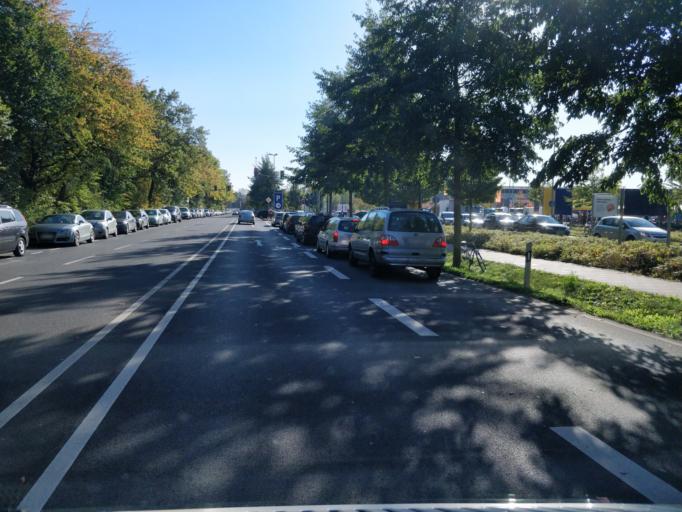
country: DE
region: North Rhine-Westphalia
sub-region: Regierungsbezirk Koln
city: Bilderstoeckchen
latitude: 50.9859
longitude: 6.9009
